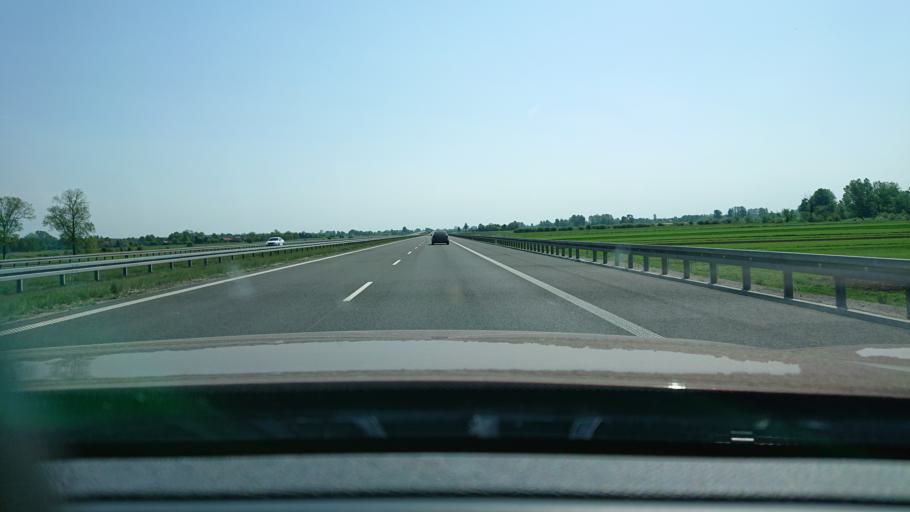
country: PL
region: Subcarpathian Voivodeship
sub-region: Powiat lancucki
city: Bialobrzegi
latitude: 50.1144
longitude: 22.3479
